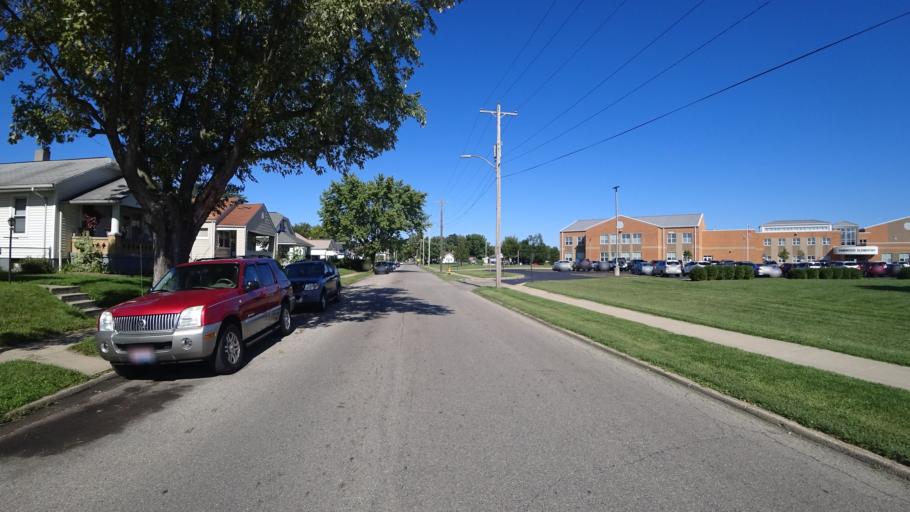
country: US
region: Ohio
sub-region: Butler County
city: Hamilton
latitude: 39.3957
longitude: -84.5424
